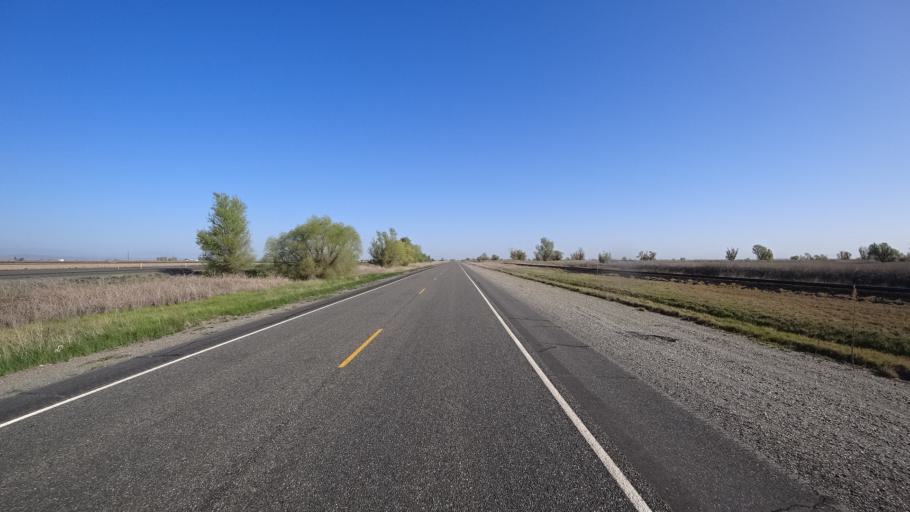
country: US
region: California
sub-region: Colusa County
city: Maxwell
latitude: 39.3931
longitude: -122.1924
